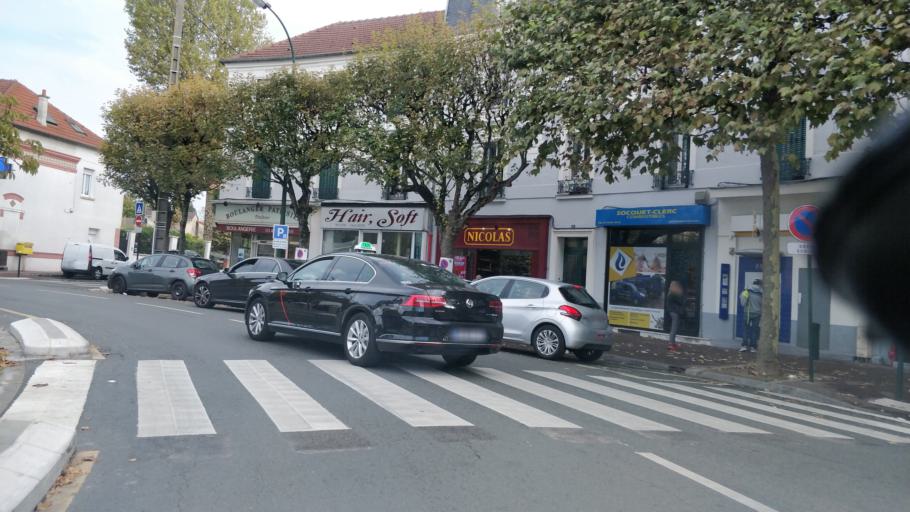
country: FR
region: Ile-de-France
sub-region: Departement de Seine-Saint-Denis
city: Le Raincy
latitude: 48.8956
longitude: 2.5265
